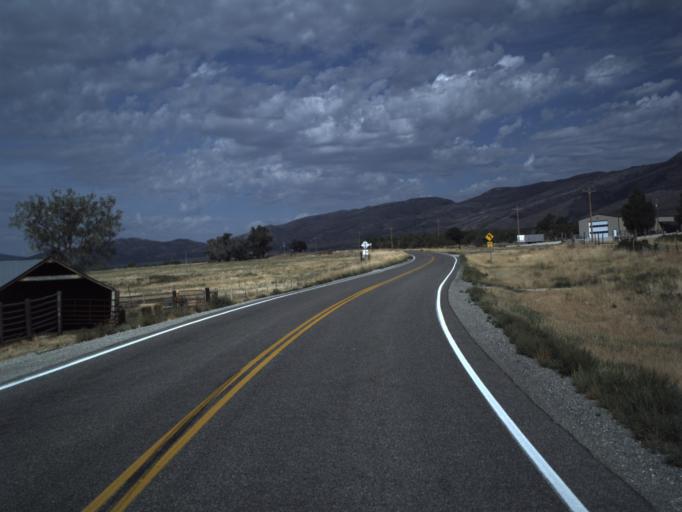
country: US
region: Idaho
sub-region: Cassia County
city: Burley
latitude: 41.8186
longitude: -113.4189
